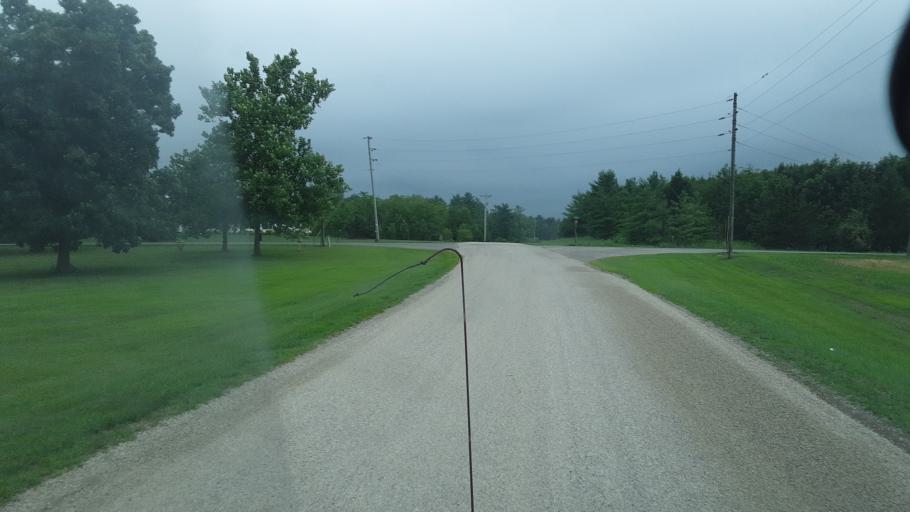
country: US
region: Indiana
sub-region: Adams County
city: Berne
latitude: 40.6423
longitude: -84.9933
